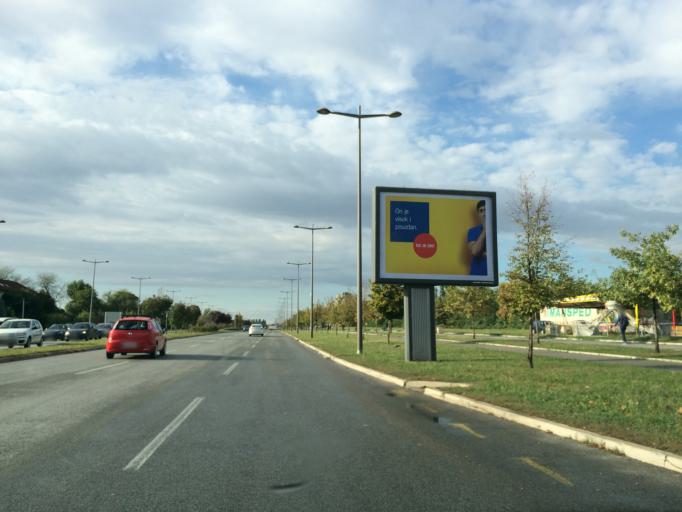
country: RS
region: Autonomna Pokrajina Vojvodina
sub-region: Juznobacki Okrug
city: Novi Sad
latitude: 45.2492
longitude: 19.8164
